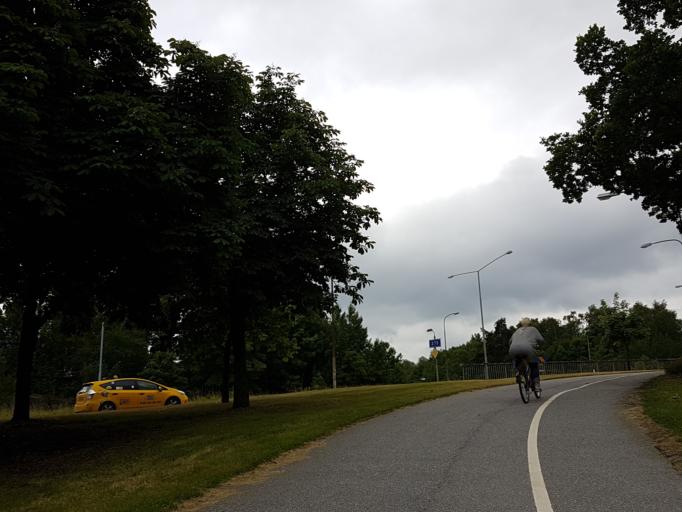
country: SE
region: Stockholm
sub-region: Solna Kommun
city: Rasunda
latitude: 59.3552
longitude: 17.9813
